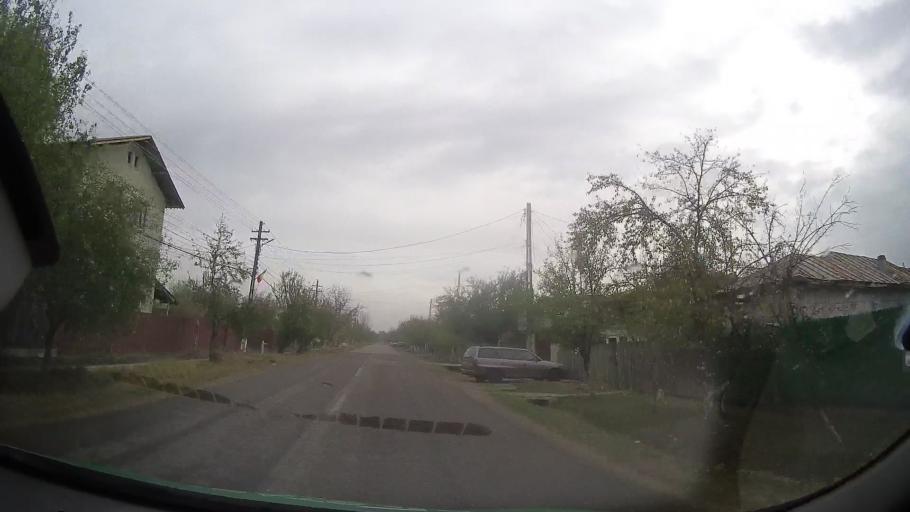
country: RO
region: Prahova
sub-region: Comuna Dumbrava
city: Dumbrava
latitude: 44.8670
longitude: 26.1992
